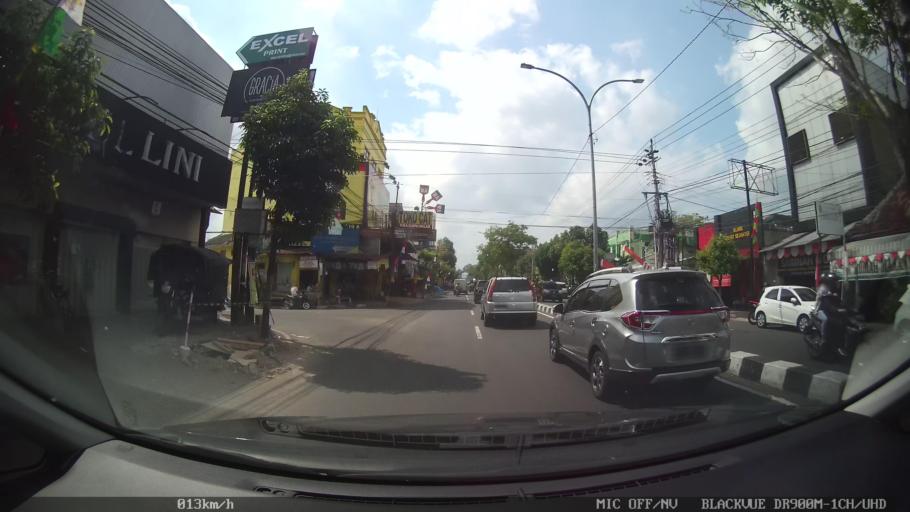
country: ID
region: Daerah Istimewa Yogyakarta
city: Yogyakarta
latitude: -7.7733
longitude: 110.3612
